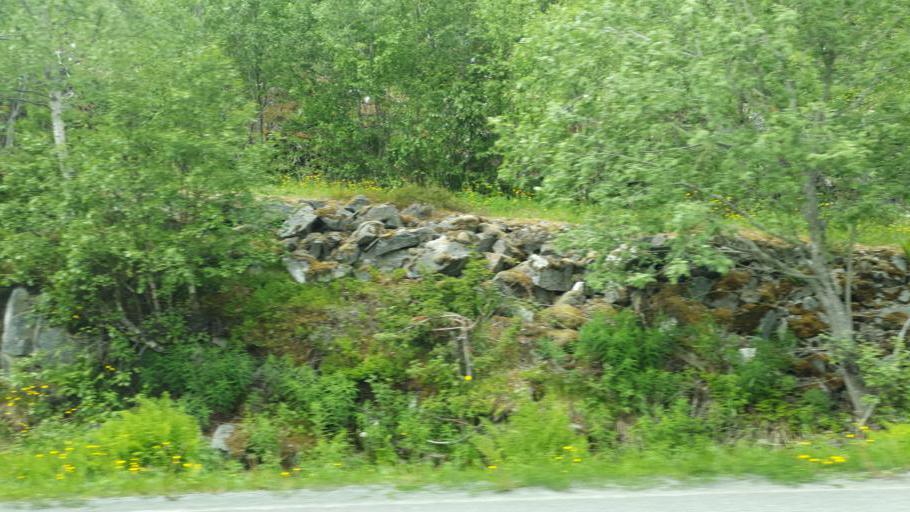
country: NO
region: Nord-Trondelag
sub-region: Leksvik
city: Leksvik
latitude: 63.6505
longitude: 10.6079
